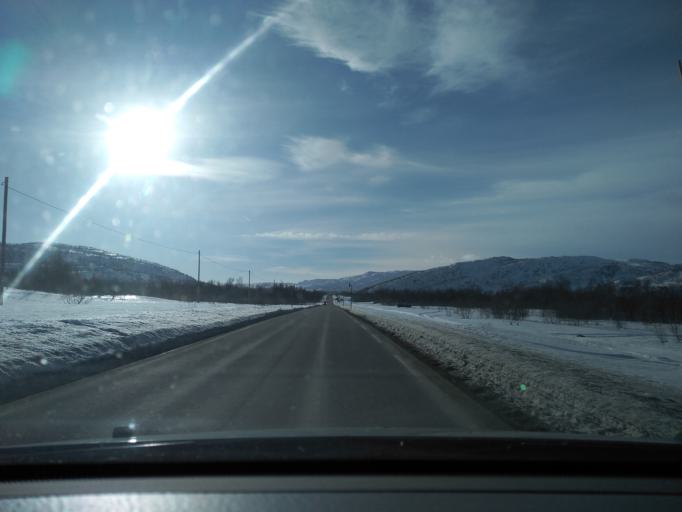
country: NO
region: Aust-Agder
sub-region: Bykle
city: Hovden
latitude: 59.6504
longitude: 7.4759
